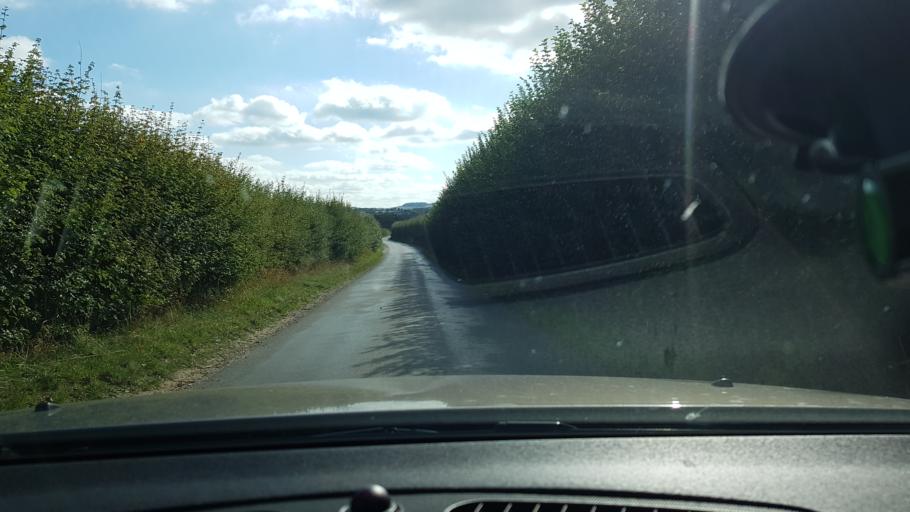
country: GB
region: England
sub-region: West Berkshire
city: Kintbury
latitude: 51.4188
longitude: -1.4464
